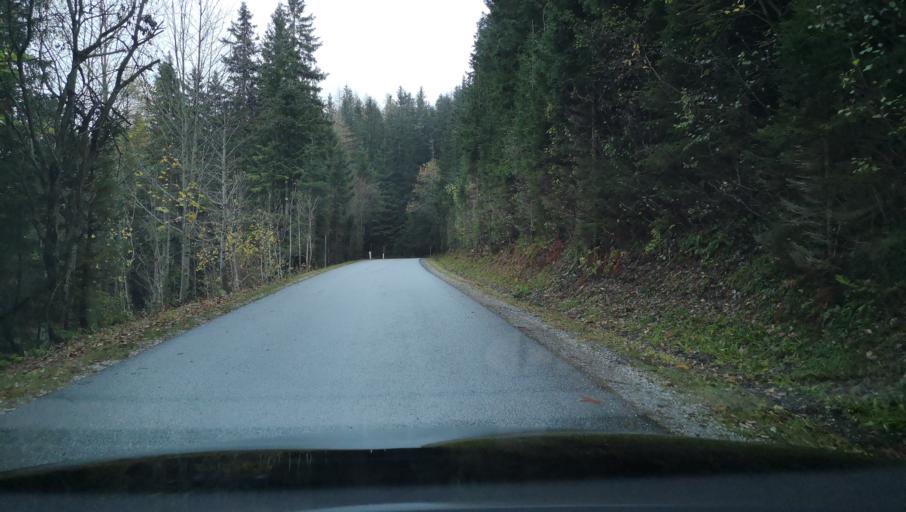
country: AT
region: Styria
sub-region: Politischer Bezirk Weiz
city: Gasen
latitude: 47.3584
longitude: 15.5859
